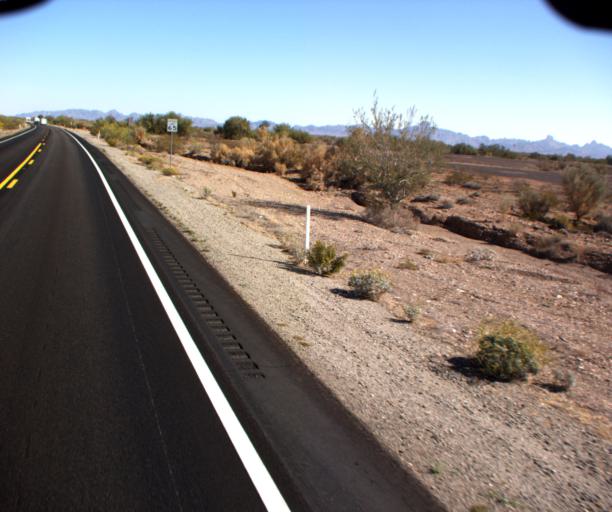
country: US
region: Arizona
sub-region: Yuma County
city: Wellton
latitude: 32.9650
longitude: -114.2920
